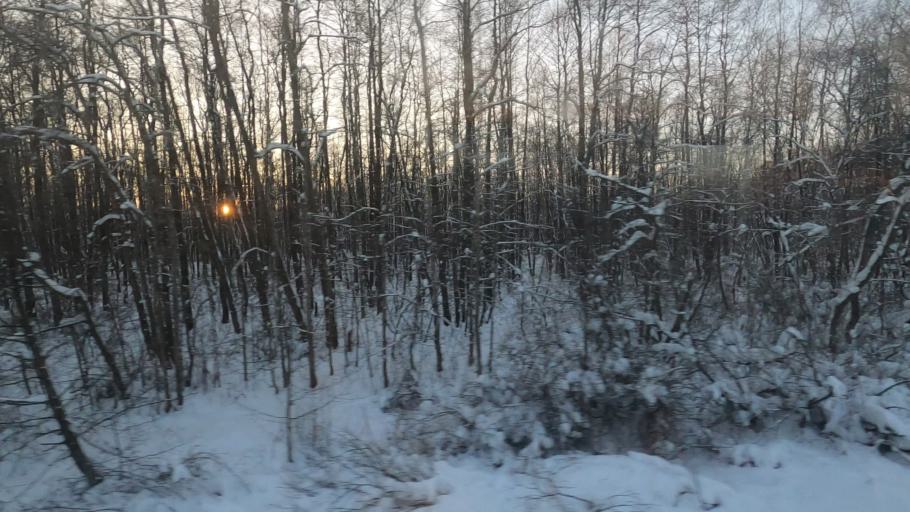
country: RU
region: Moskovskaya
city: Dmitrov
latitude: 56.3721
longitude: 37.5245
